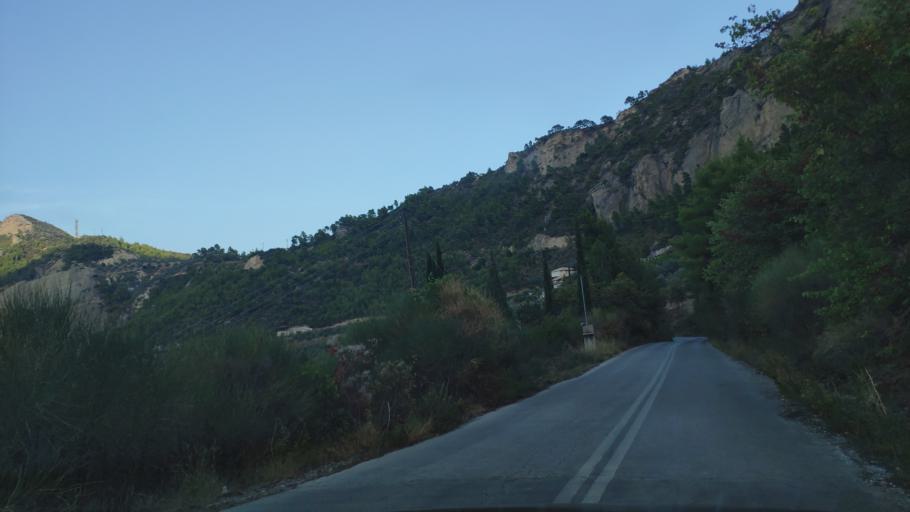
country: GR
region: West Greece
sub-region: Nomos Achaias
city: Aiyira
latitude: 38.0955
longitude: 22.3995
